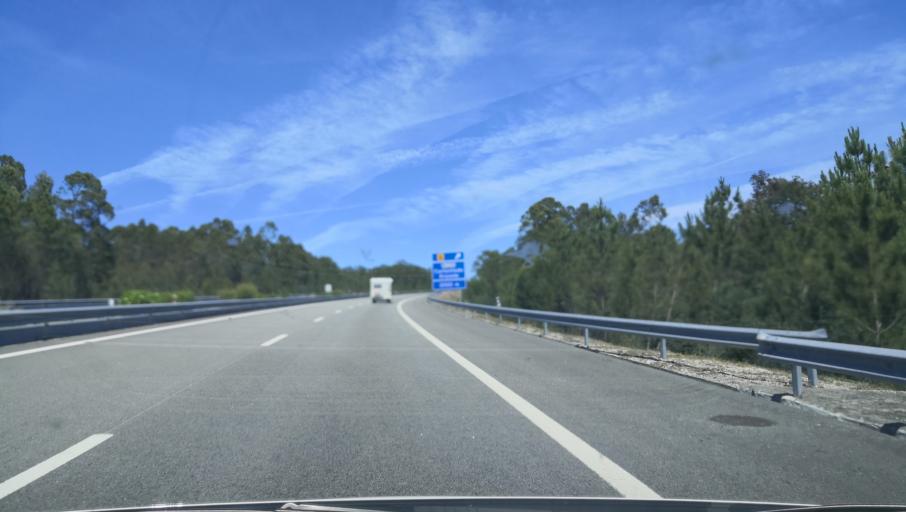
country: PT
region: Coimbra
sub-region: Montemor-O-Velho
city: Arazede
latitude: 40.2480
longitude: -8.6539
